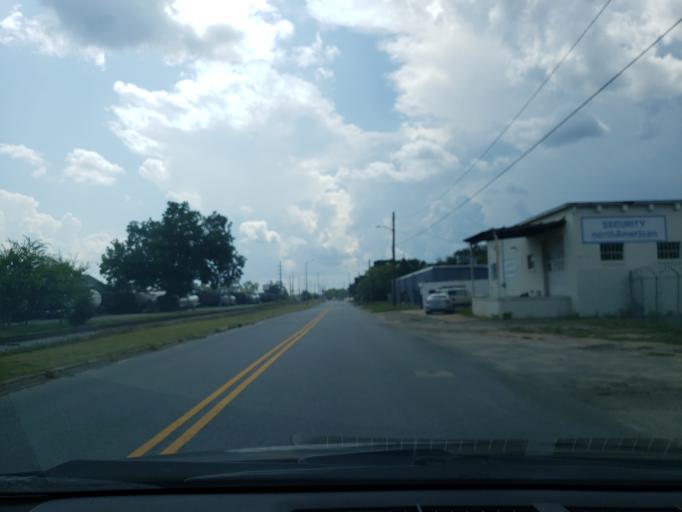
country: US
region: Georgia
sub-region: Dougherty County
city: Albany
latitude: 31.5811
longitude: -84.1705
